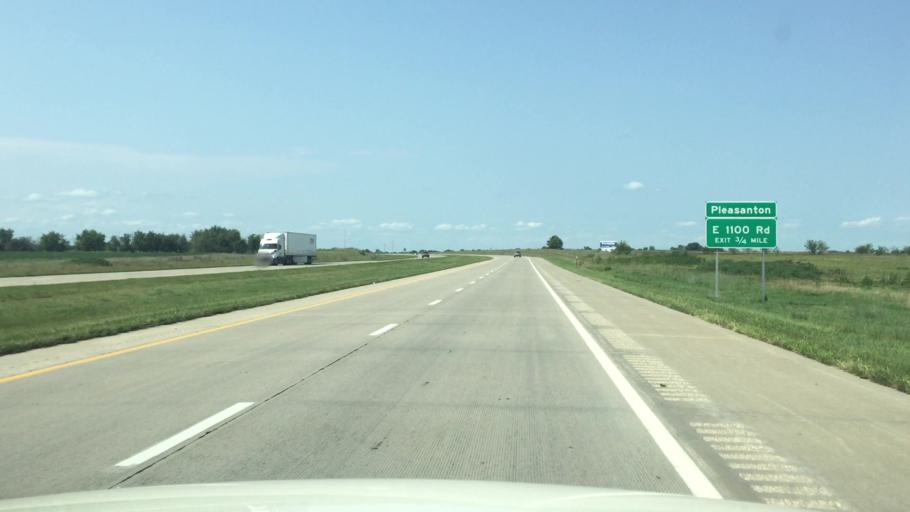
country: US
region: Kansas
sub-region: Linn County
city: Pleasanton
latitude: 38.1694
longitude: -94.6957
